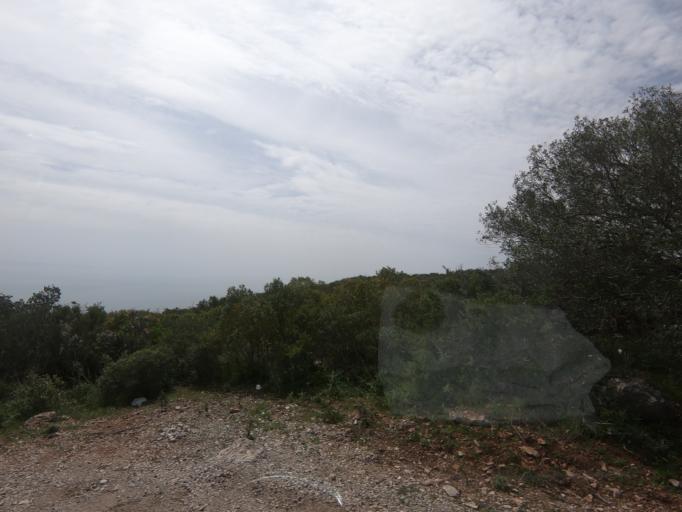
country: PT
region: Setubal
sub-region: Setubal
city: Setubal
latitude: 38.4897
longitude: -8.9529
